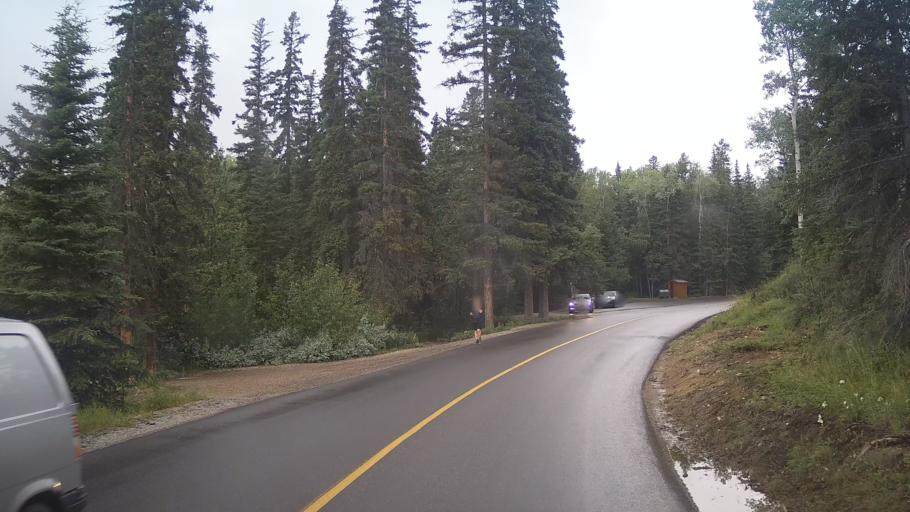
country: CA
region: Alberta
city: Jasper Park Lodge
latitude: 52.9104
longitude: -118.0917
